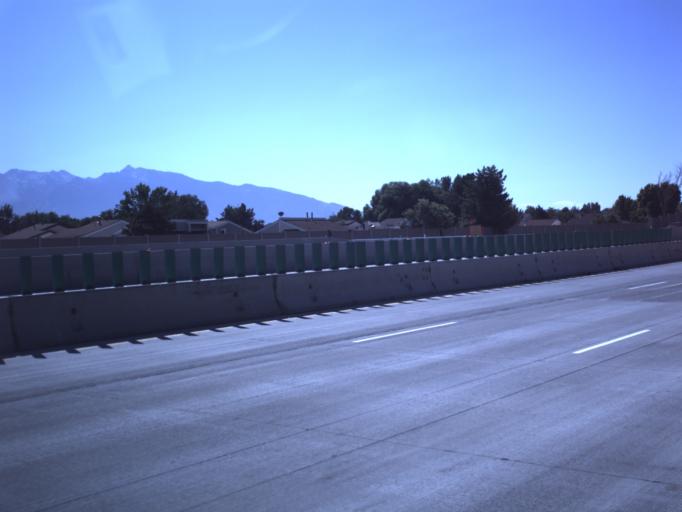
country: US
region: Utah
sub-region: Salt Lake County
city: Taylorsville
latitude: 40.6804
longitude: -111.9520
